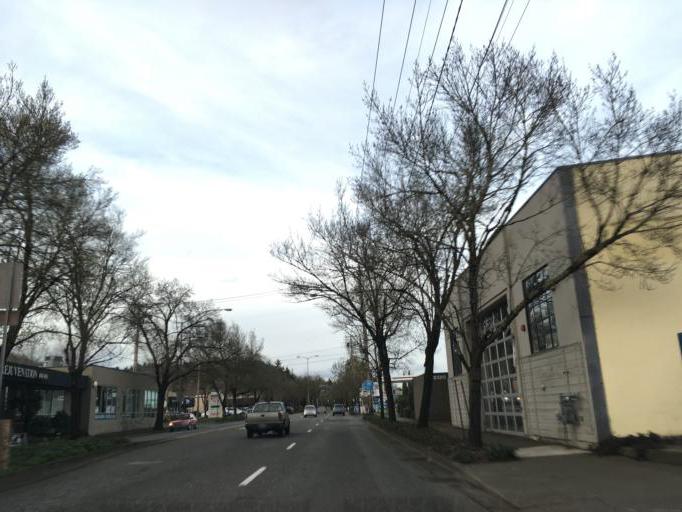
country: US
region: Oregon
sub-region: Multnomah County
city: Portland
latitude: 45.4780
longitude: -122.6723
